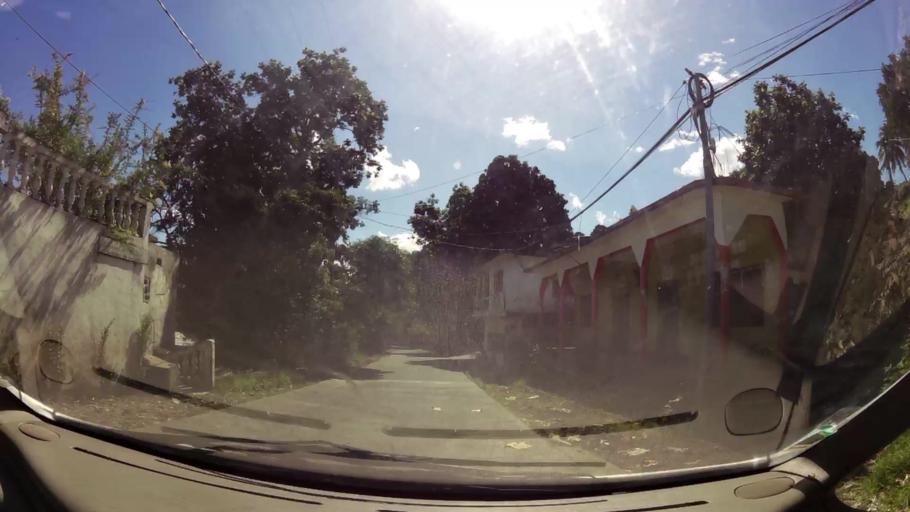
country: KM
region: Grande Comore
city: Moroni
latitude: -11.7073
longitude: 43.2570
